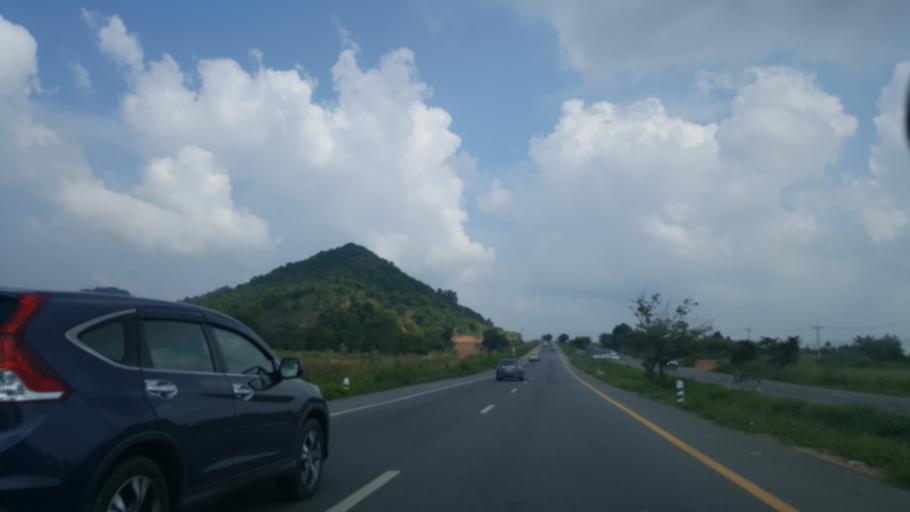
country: TH
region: Rayong
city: Ban Chang
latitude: 12.7474
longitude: 100.9910
